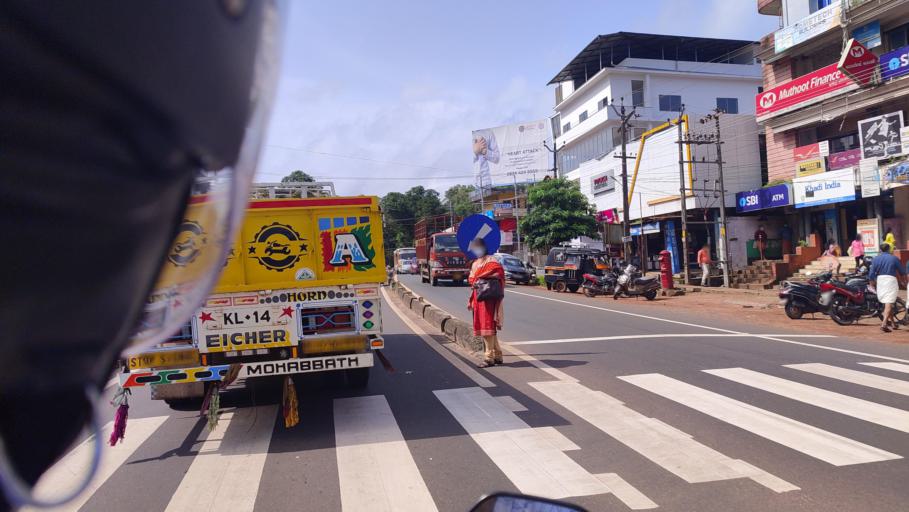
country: IN
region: Kerala
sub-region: Kasaragod District
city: Nileshwar
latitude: 12.2166
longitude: 75.1625
